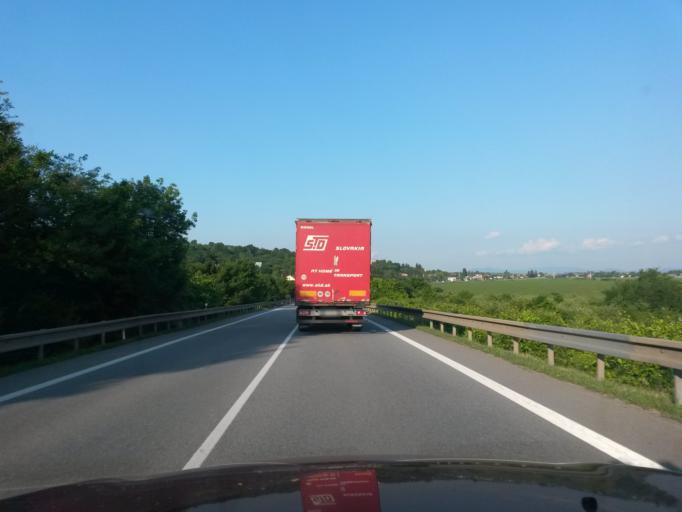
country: SK
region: Kosicky
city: Moldava nad Bodvou
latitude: 48.6079
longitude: 20.9742
